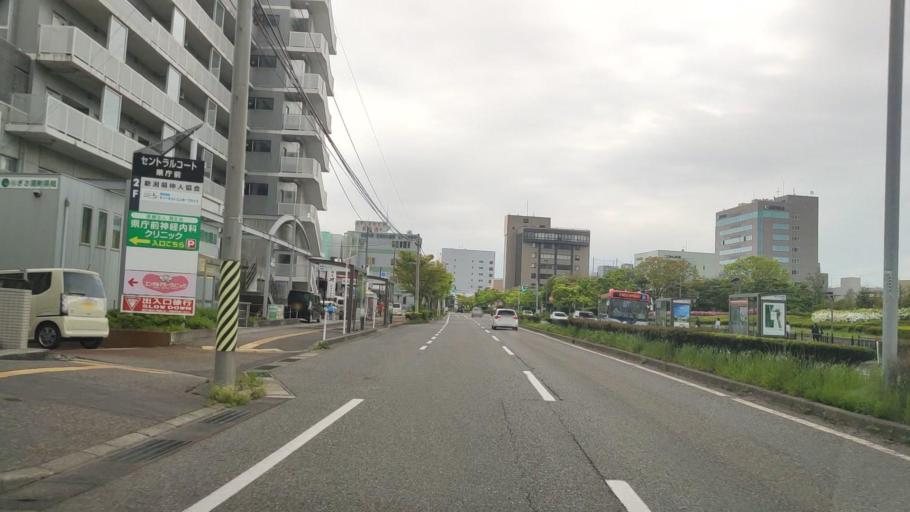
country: JP
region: Niigata
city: Niigata-shi
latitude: 37.9016
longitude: 139.0246
